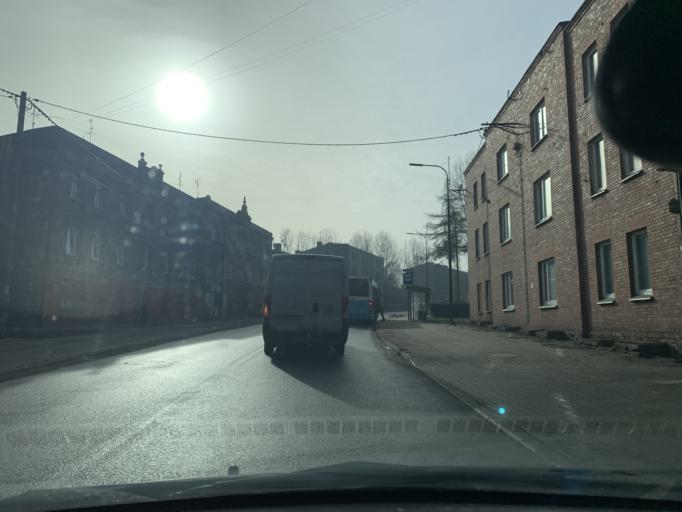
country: PL
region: Silesian Voivodeship
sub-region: Ruda Slaska
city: Ruda Slaska
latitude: 50.3228
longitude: 18.8568
